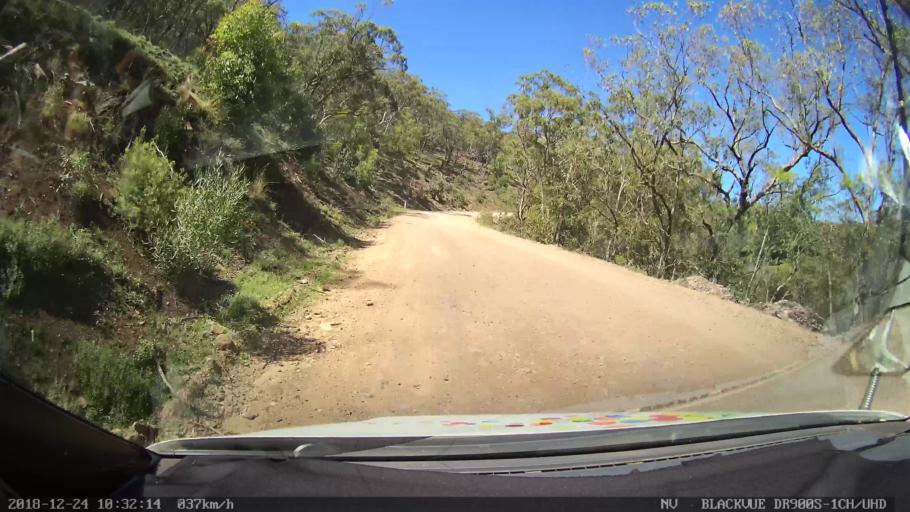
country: AU
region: New South Wales
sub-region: Upper Hunter Shire
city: Merriwa
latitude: -31.8407
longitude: 150.5171
